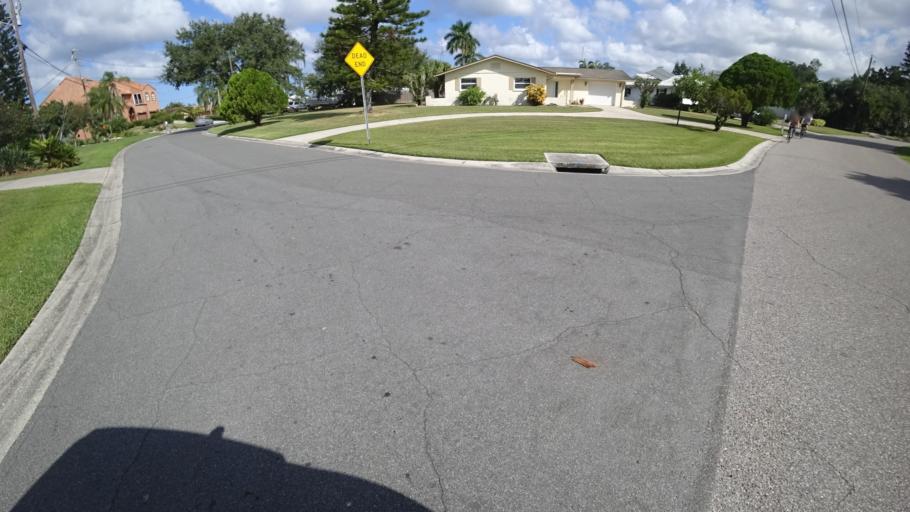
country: US
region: Florida
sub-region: Manatee County
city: Memphis
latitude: 27.5570
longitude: -82.5723
